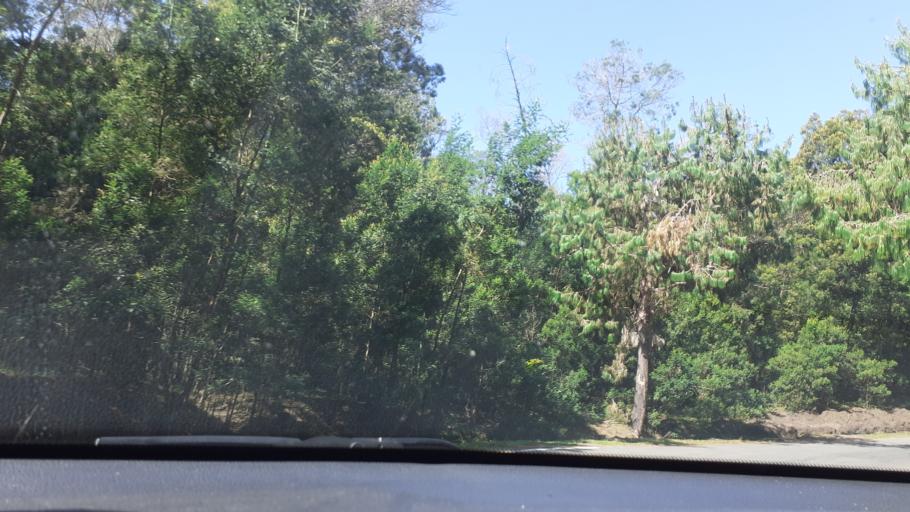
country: IN
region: Tamil Nadu
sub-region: Dindigul
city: Kodaikanal
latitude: 10.2195
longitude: 77.4226
